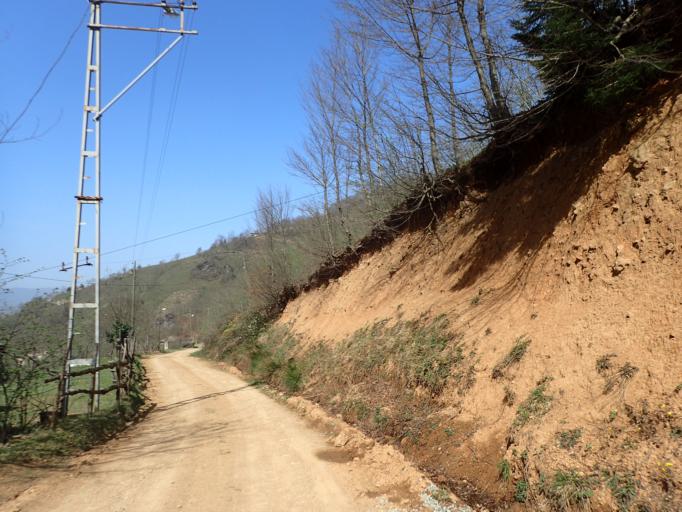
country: TR
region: Ordu
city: Kabaduz
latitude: 40.8250
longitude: 37.8763
